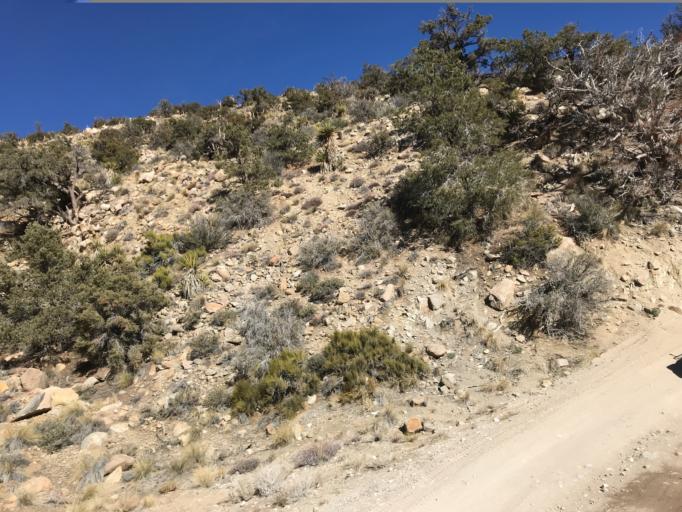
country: US
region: California
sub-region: San Bernardino County
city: Big Bear City
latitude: 34.2338
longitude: -116.6839
